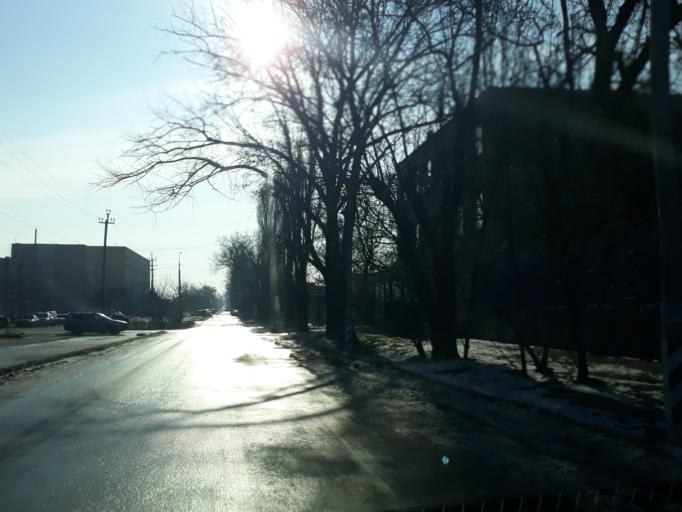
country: RU
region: Rostov
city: Taganrog
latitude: 47.2270
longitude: 38.9069
